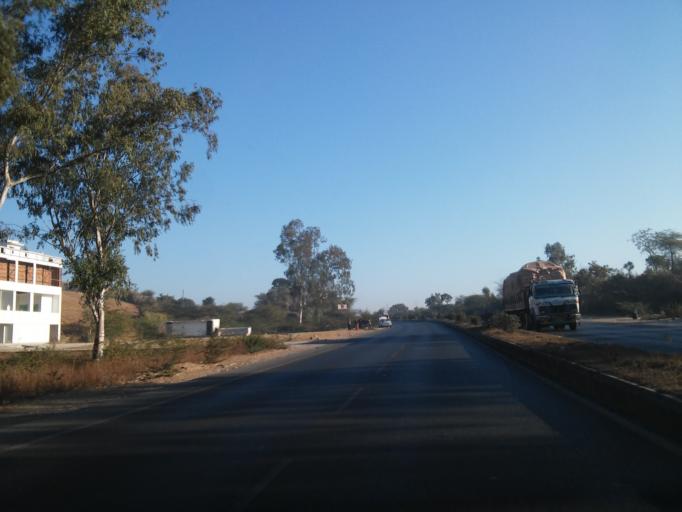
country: IN
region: Rajasthan
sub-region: Dungarpur
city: Dungarpur
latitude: 23.8796
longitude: 73.5321
